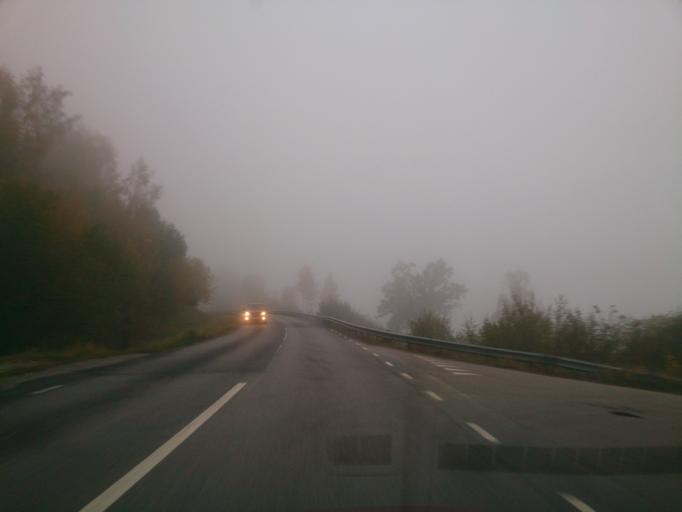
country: SE
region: OEstergoetland
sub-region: Kinda Kommun
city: Rimforsa
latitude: 58.0900
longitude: 15.8545
